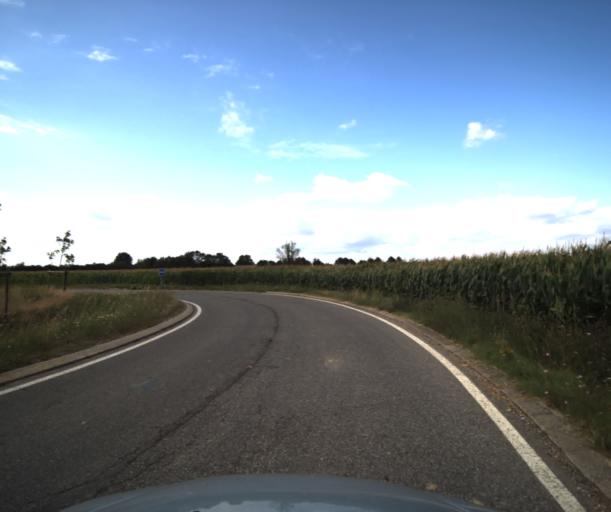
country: FR
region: Midi-Pyrenees
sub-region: Departement de la Haute-Garonne
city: Le Fauga
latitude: 43.4164
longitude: 1.3010
